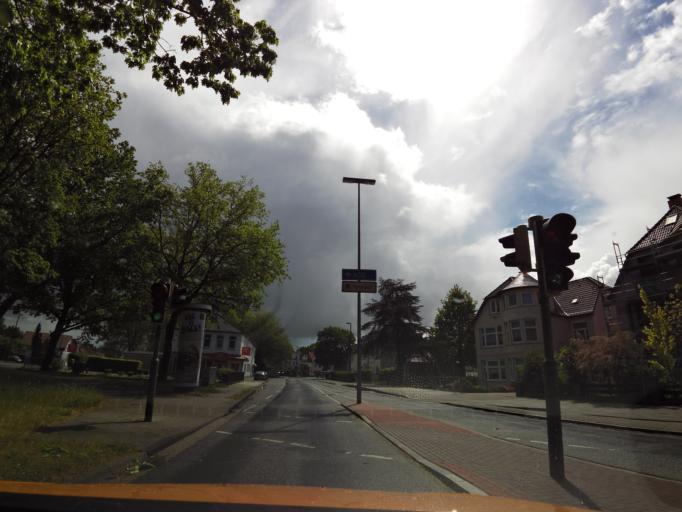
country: DE
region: Lower Saxony
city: Delmenhorst
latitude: 53.0445
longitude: 8.6376
